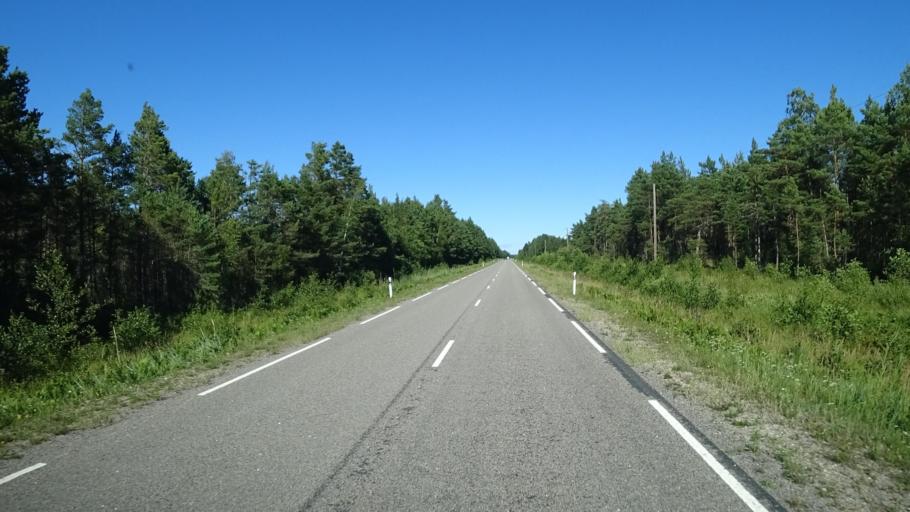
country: LV
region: Dundaga
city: Dundaga
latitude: 57.7025
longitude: 22.4250
